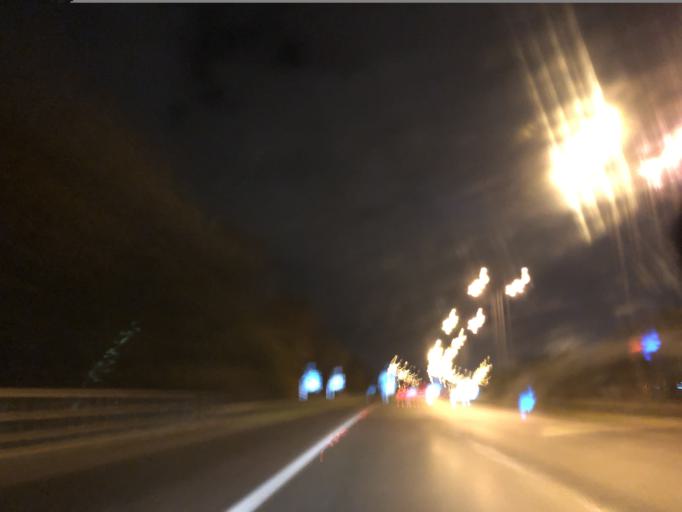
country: GB
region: England
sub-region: Kirklees
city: Cleckheaton
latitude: 53.7506
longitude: -1.7397
